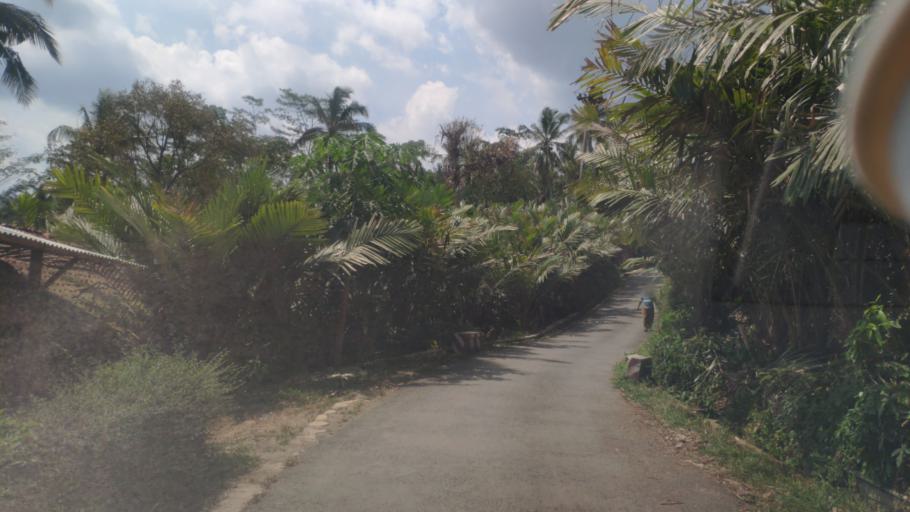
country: ID
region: Central Java
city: Wonosobo
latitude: -7.3586
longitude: 109.7800
